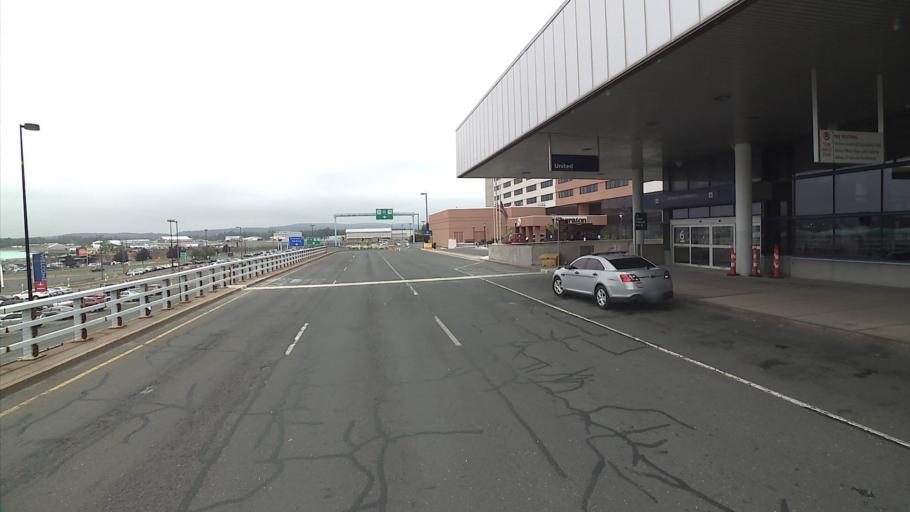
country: US
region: Connecticut
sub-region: Hartford County
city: Windsor Locks
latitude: 41.9302
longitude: -72.6858
